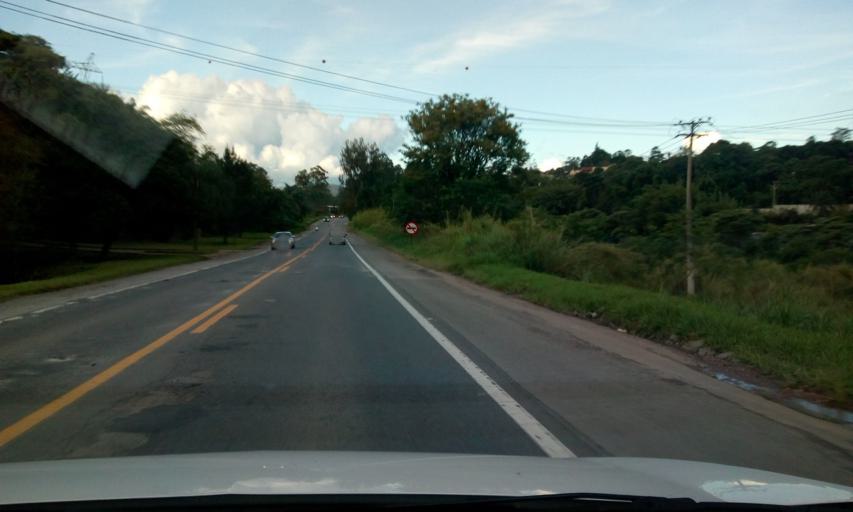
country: BR
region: Sao Paulo
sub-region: Itatiba
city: Itatiba
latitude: -22.9982
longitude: -46.8071
